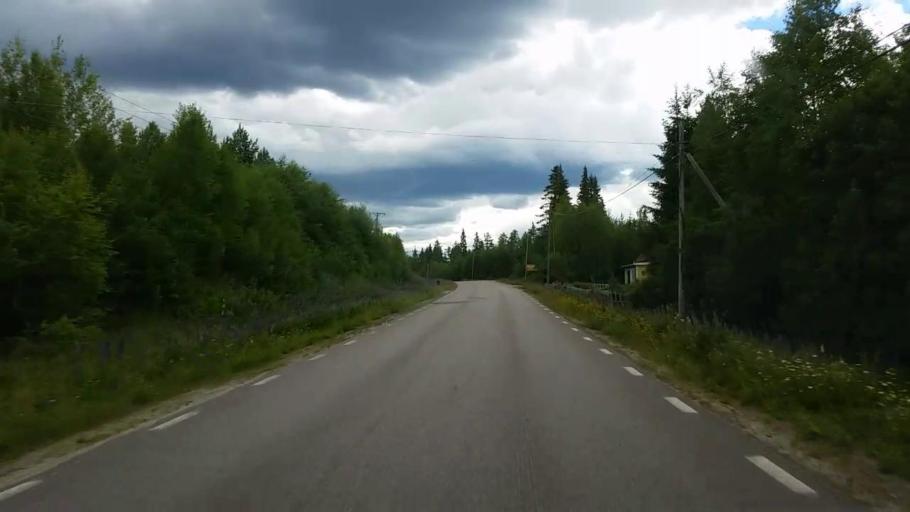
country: SE
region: Gaevleborg
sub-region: Ovanakers Kommun
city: Edsbyn
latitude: 61.4584
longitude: 15.8757
